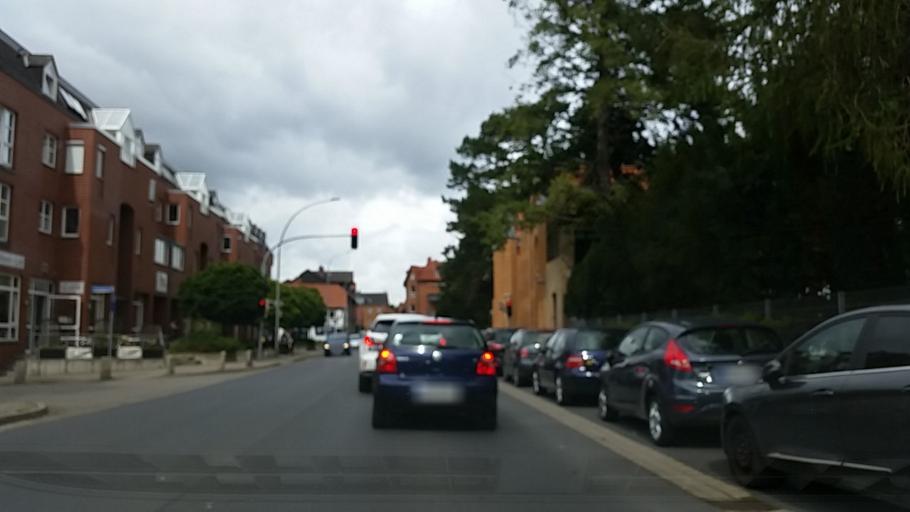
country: DE
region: Lower Saxony
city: Wolfenbuettel
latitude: 52.1612
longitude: 10.5477
